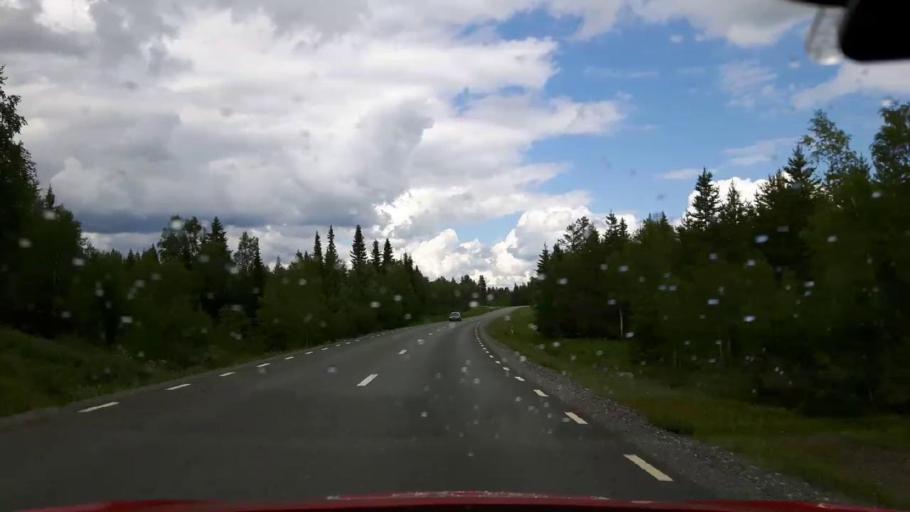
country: SE
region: Jaemtland
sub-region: Krokoms Kommun
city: Krokom
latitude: 63.5869
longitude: 14.2939
